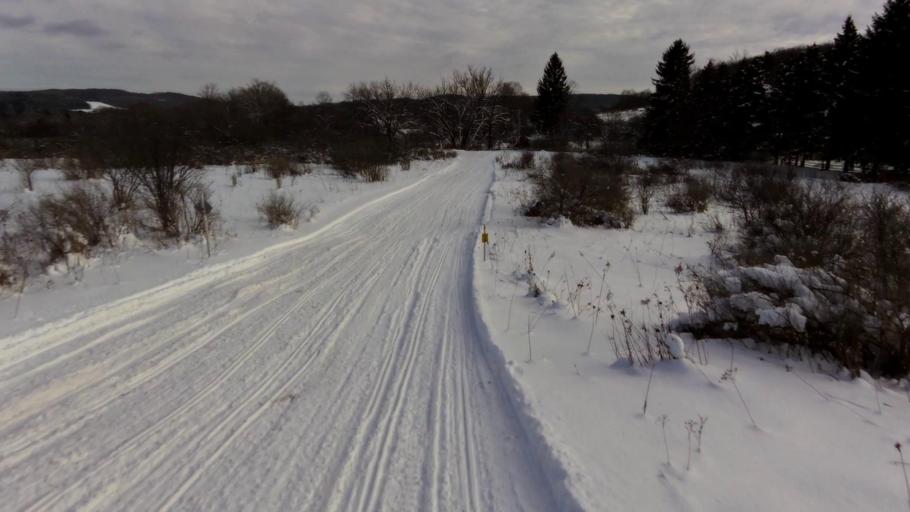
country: US
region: New York
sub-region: Cattaraugus County
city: Franklinville
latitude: 42.3388
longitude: -78.4731
